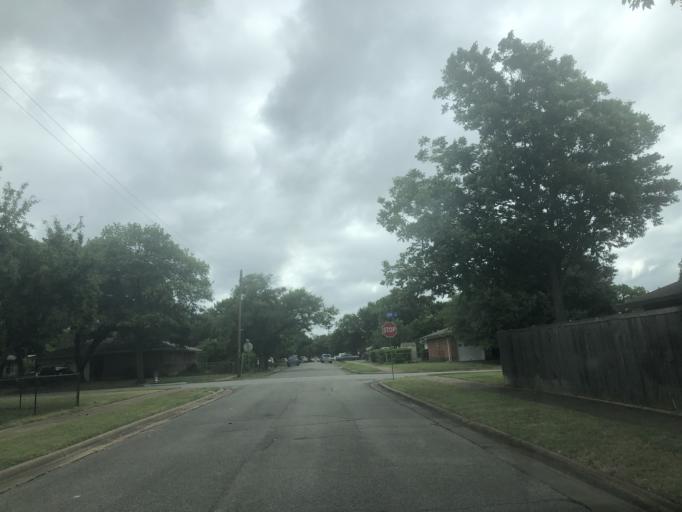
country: US
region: Texas
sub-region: Dallas County
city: Duncanville
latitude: 32.6526
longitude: -96.9166
